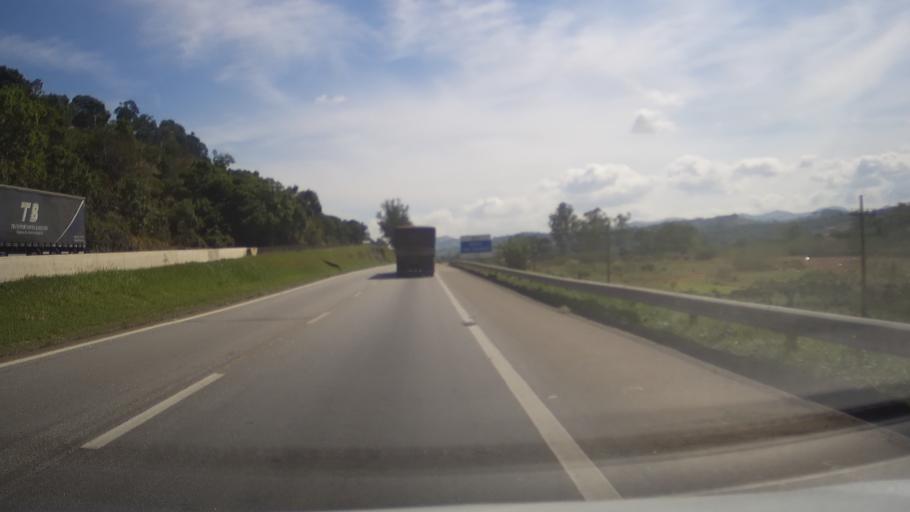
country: BR
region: Minas Gerais
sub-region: Cambui
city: Cambui
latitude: -22.5896
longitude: -46.0520
